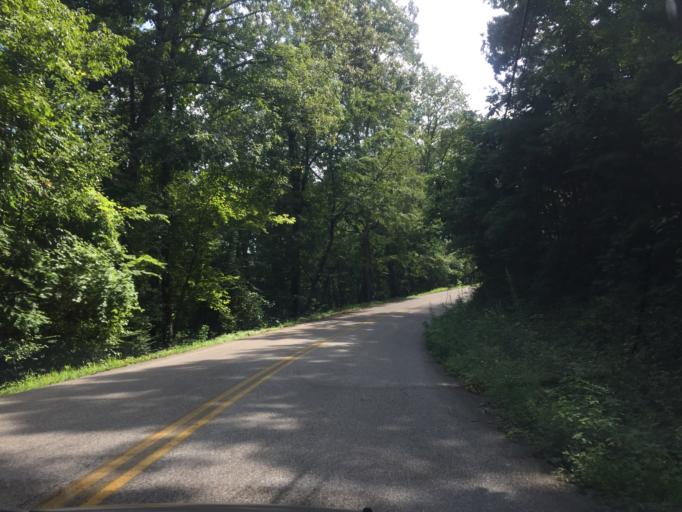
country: US
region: Tennessee
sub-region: Hamilton County
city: Harrison
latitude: 35.0973
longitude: -85.1940
